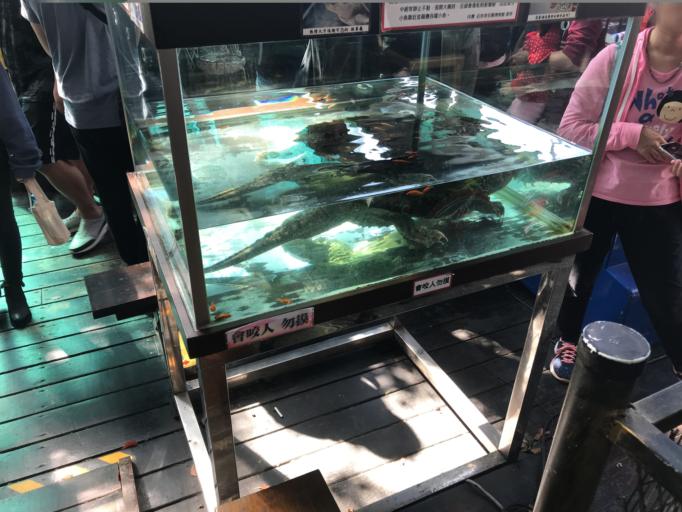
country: TW
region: Taiwan
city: Daxi
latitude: 24.7055
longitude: 121.1810
